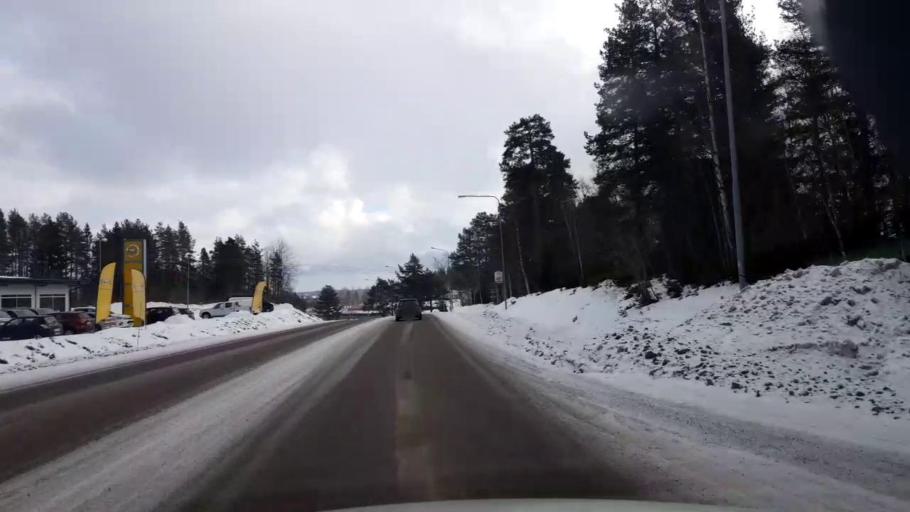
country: SE
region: Gaevleborg
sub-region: Hudiksvalls Kommun
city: Hudiksvall
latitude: 61.7378
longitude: 17.0886
